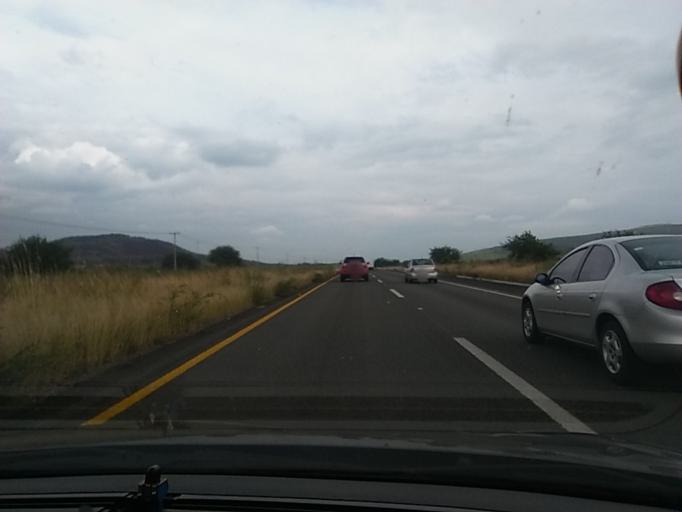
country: MX
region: Michoacan
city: Ecuandureo
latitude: 20.1746
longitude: -102.1823
